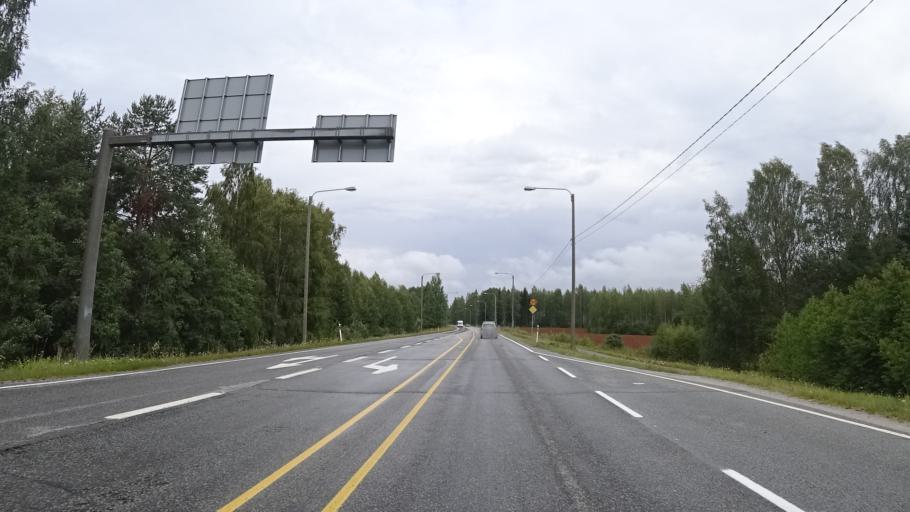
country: FI
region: Southern Savonia
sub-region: Savonlinna
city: Kerimaeki
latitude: 61.9267
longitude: 29.2712
